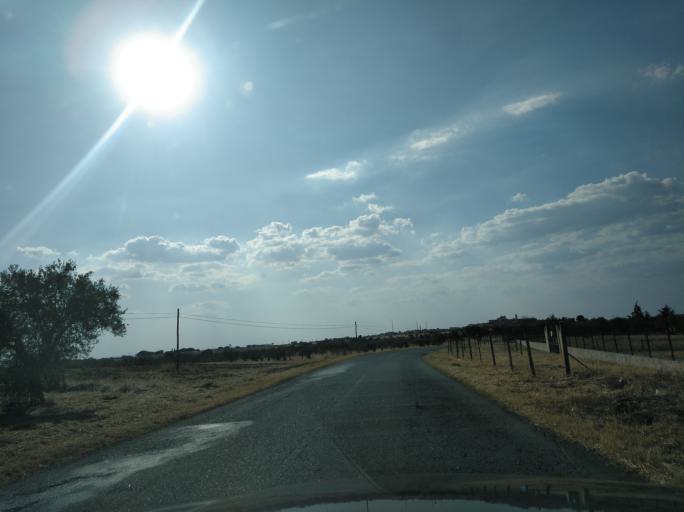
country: PT
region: Evora
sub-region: Mourao
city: Mourao
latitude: 38.3763
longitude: -7.3261
